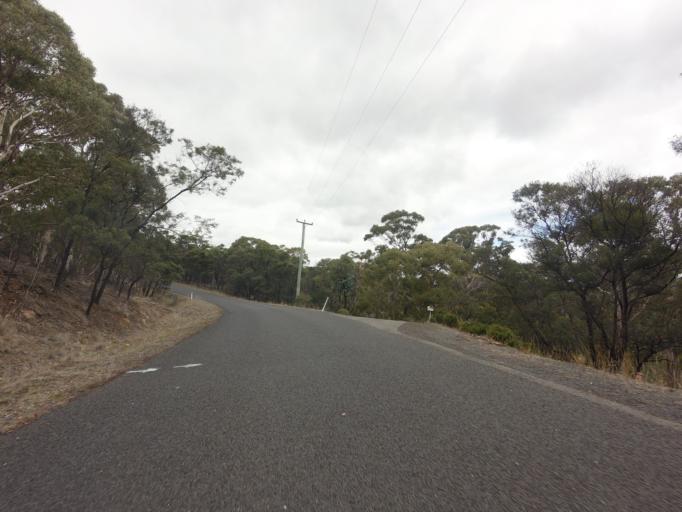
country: AU
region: Tasmania
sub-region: Clarence
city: Cambridge
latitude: -42.7888
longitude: 147.3999
